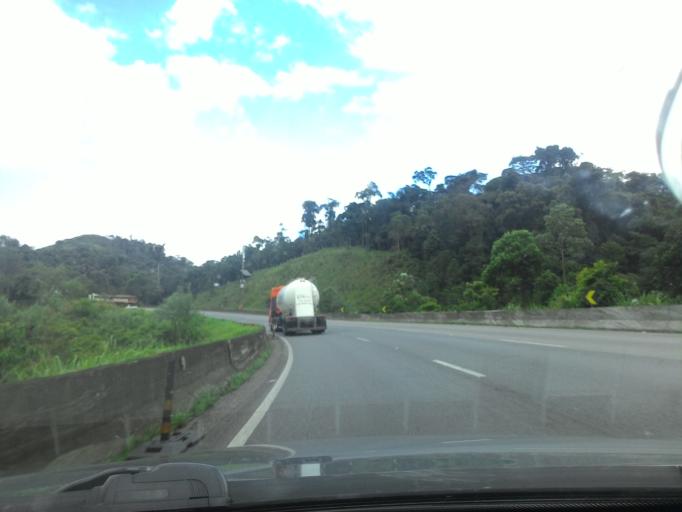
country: BR
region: Sao Paulo
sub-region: Cajati
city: Cajati
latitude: -24.9055
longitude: -48.2551
